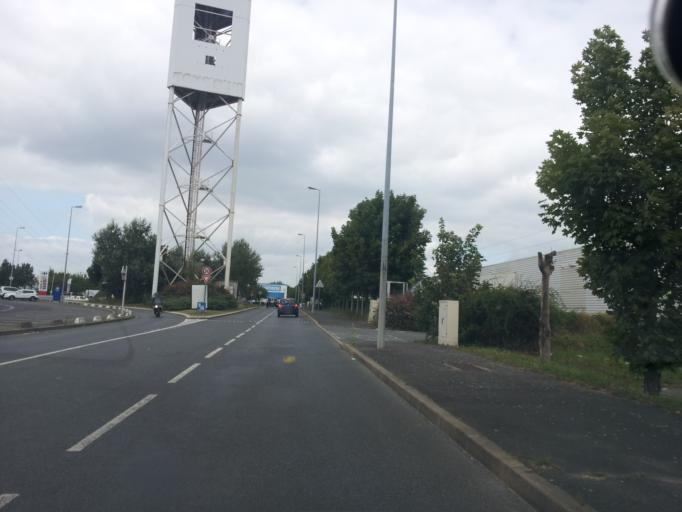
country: FR
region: Ile-de-France
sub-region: Departement de l'Essonne
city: Villabe
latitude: 48.5849
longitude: 2.4521
